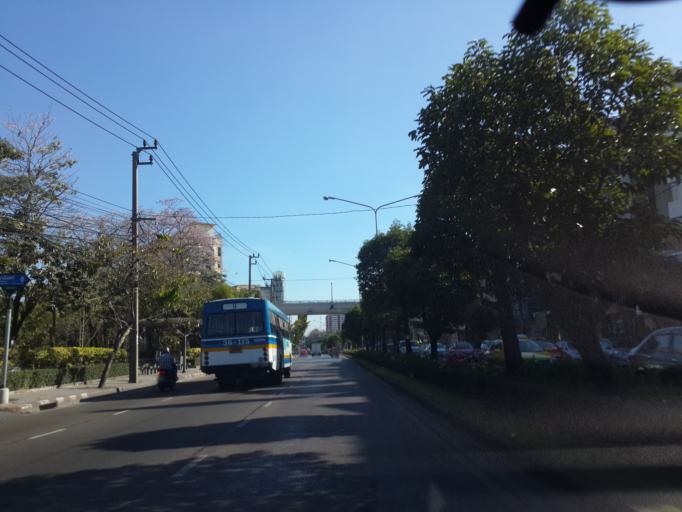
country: TH
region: Bangkok
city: Bang Kapi
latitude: 13.7705
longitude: 100.6474
